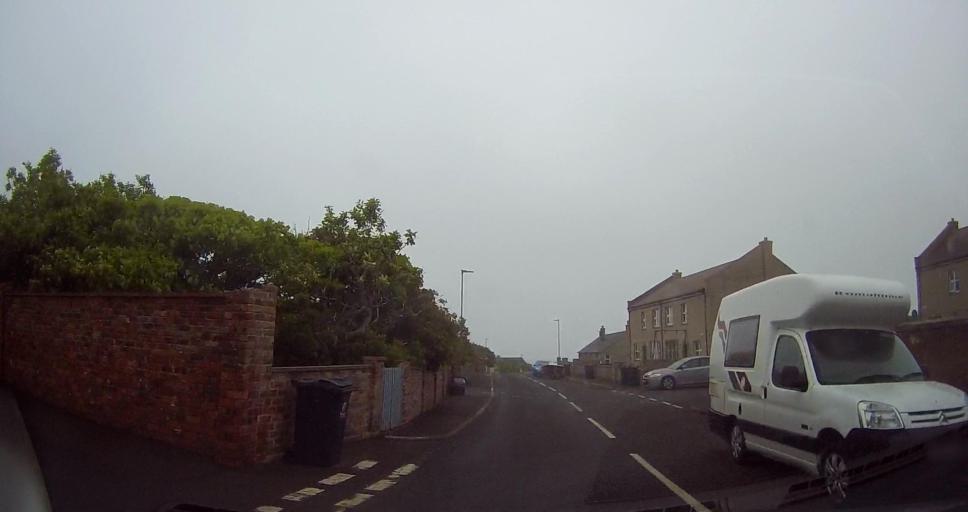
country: GB
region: Scotland
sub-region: Orkney Islands
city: Stromness
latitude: 58.9571
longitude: -3.3040
